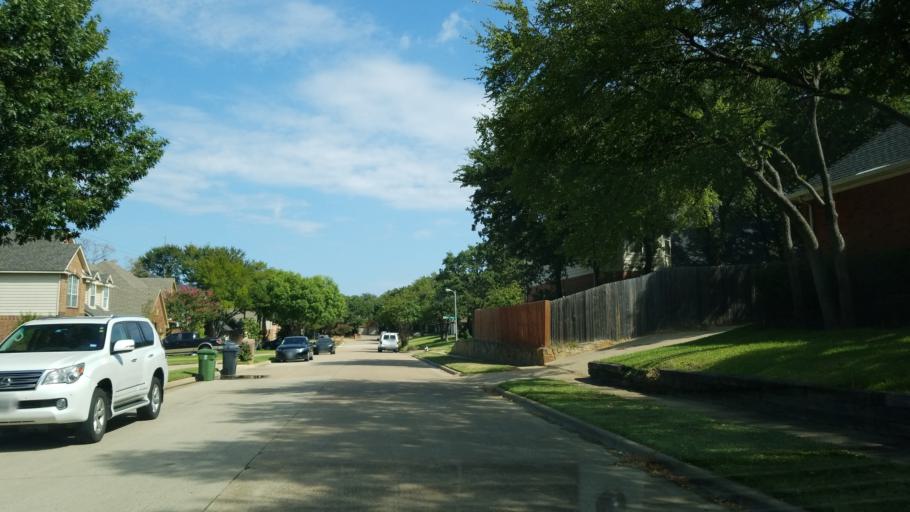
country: US
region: Texas
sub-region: Tarrant County
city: Grapevine
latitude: 32.8867
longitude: -97.0948
